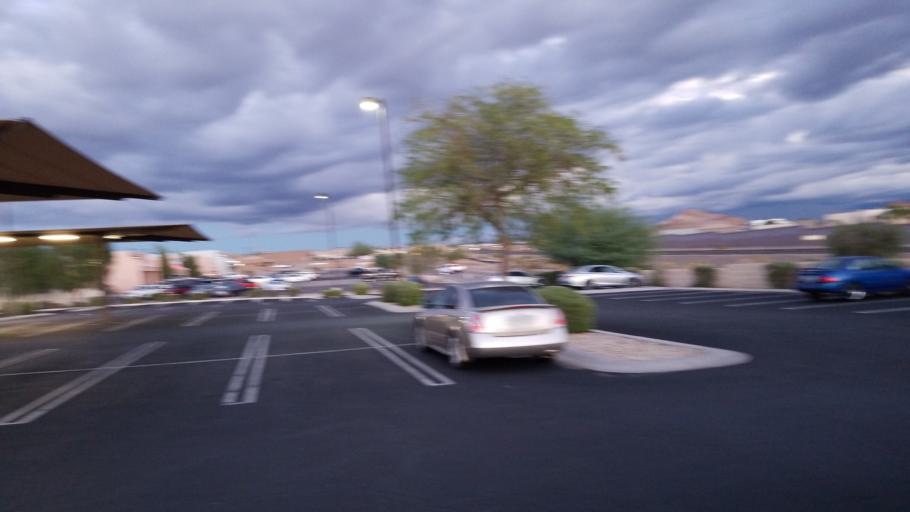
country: US
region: Arizona
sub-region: Mohave County
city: Lake Havasu City
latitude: 34.4584
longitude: -114.2789
